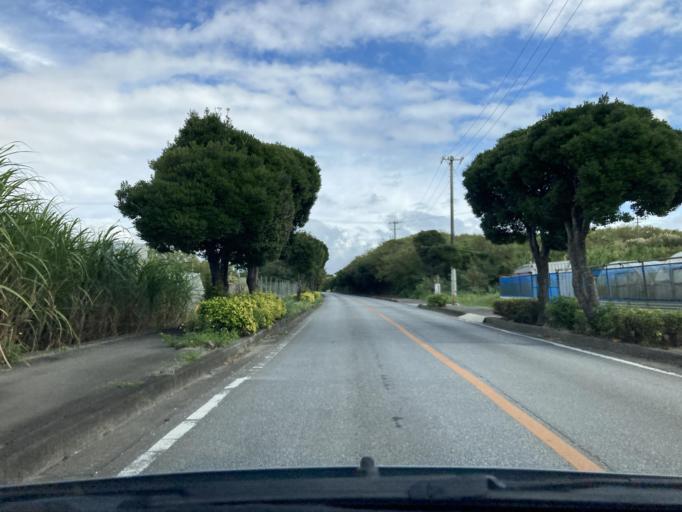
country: JP
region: Okinawa
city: Itoman
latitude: 26.1318
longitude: 127.7065
